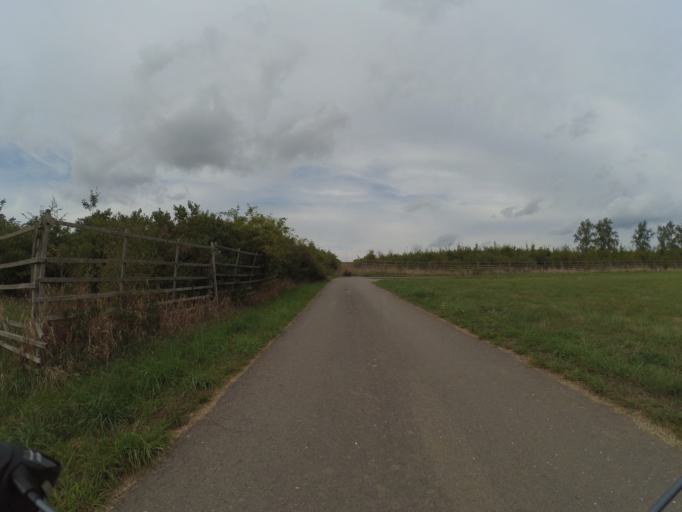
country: DE
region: Rheinland-Pfalz
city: Herforst
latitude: 49.9621
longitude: 6.6900
